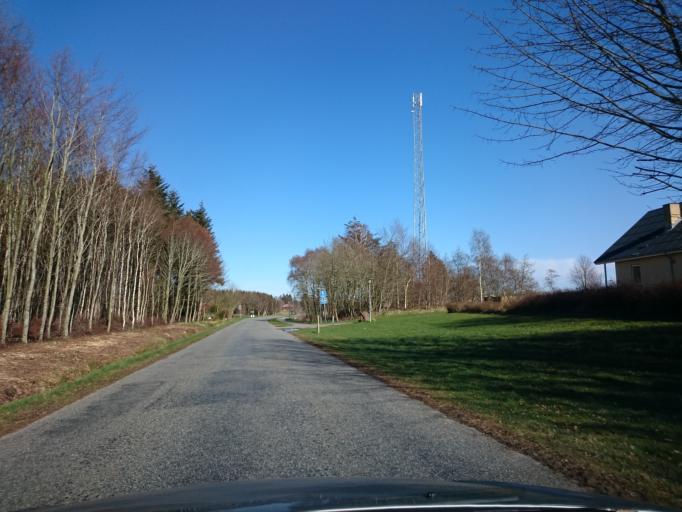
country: DK
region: North Denmark
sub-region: Hjorring Kommune
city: Sindal
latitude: 57.5657
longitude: 10.0986
